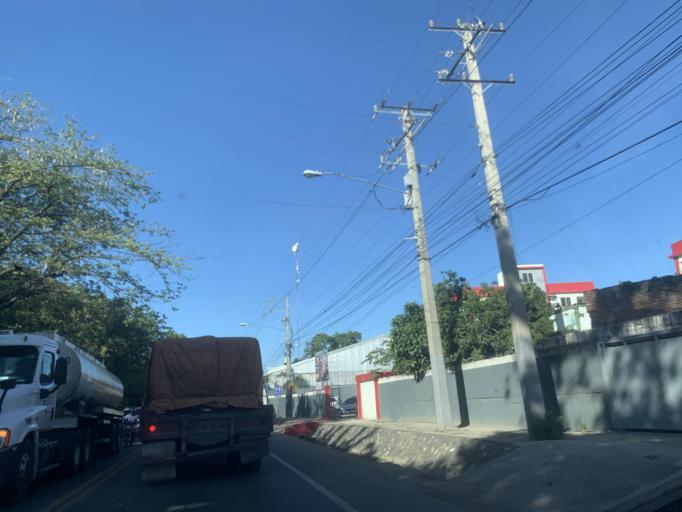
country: DO
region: San Cristobal
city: Bajos de Haina
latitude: 18.4270
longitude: -70.0351
